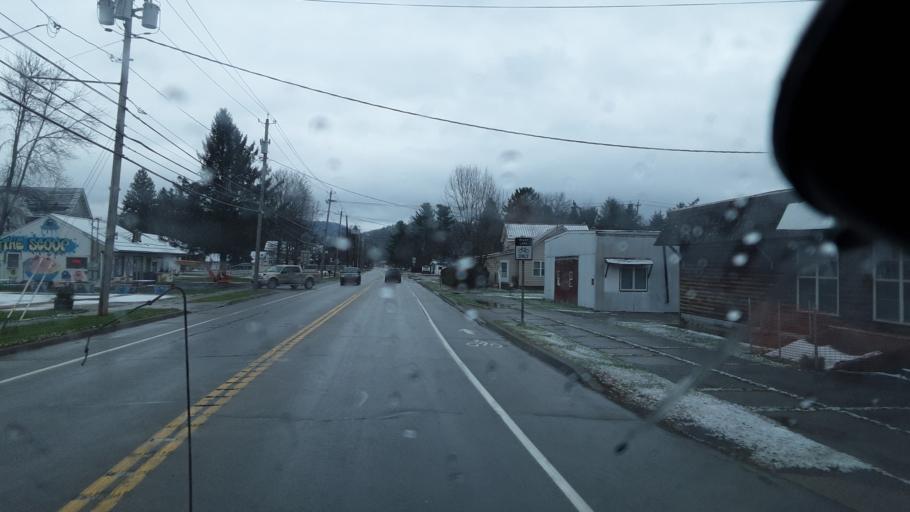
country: US
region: New York
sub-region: Cattaraugus County
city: Portville
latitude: 42.0270
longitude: -78.3383
